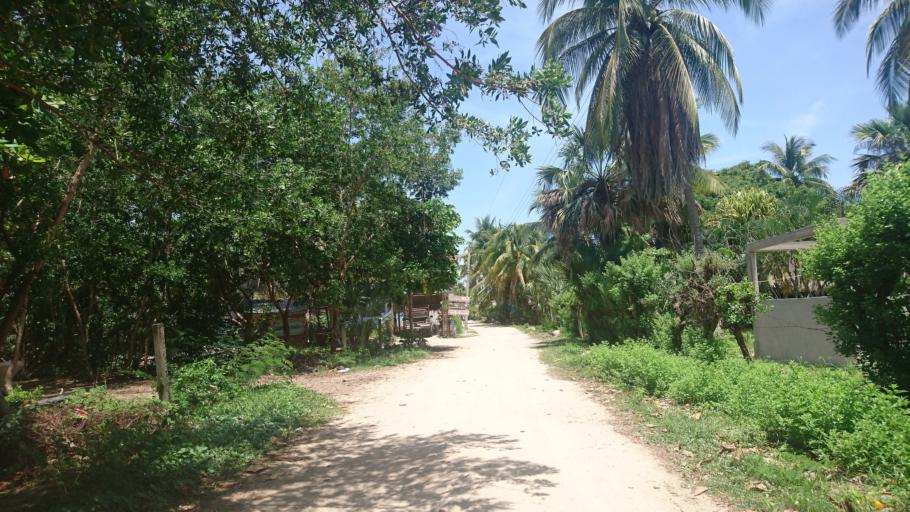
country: MX
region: Oaxaca
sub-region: Villa de Tututepec de Melchor Ocampo
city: Santa Rosa de Lima
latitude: 15.9682
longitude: -97.6784
